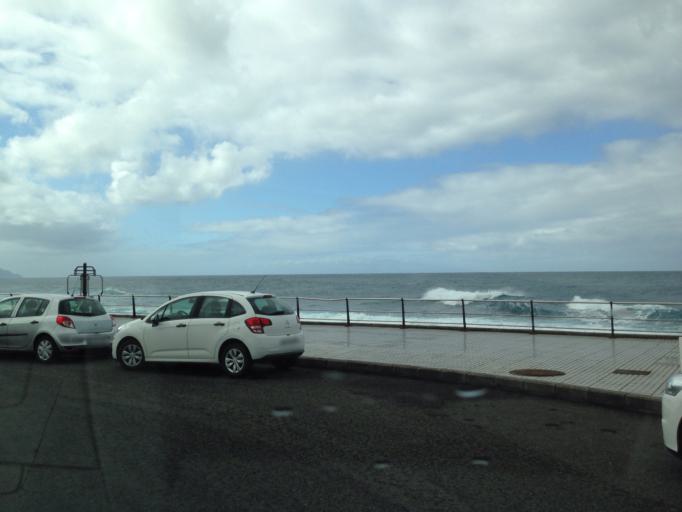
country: ES
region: Canary Islands
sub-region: Provincia de Las Palmas
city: Agaete
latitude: 28.1042
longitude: -15.7121
